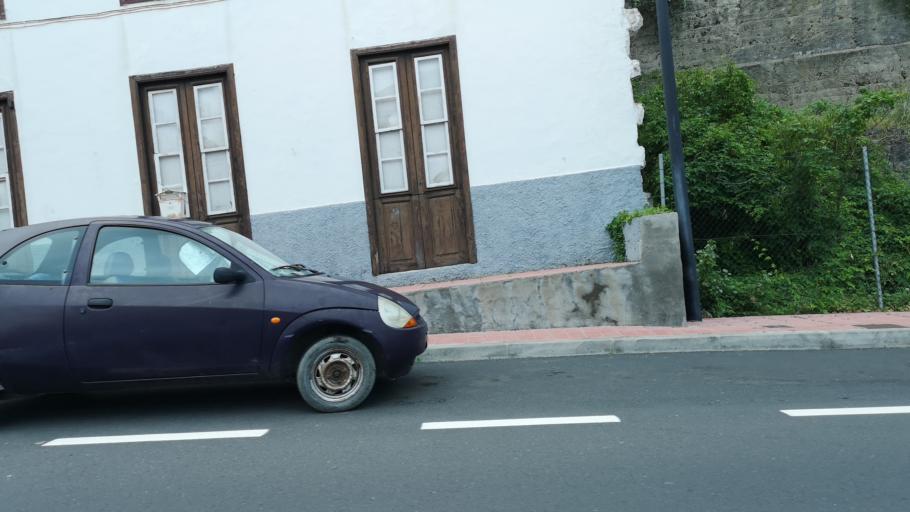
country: ES
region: Canary Islands
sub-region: Provincia de Santa Cruz de Tenerife
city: Hermigua
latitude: 28.1561
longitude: -17.1977
